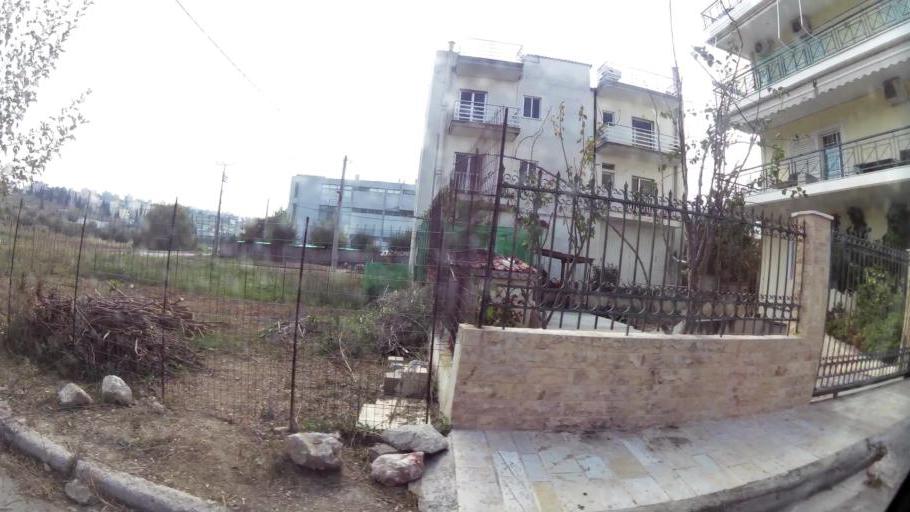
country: GR
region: Attica
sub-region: Nomarchia Dytikis Attikis
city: Zefyri
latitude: 38.0653
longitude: 23.7201
